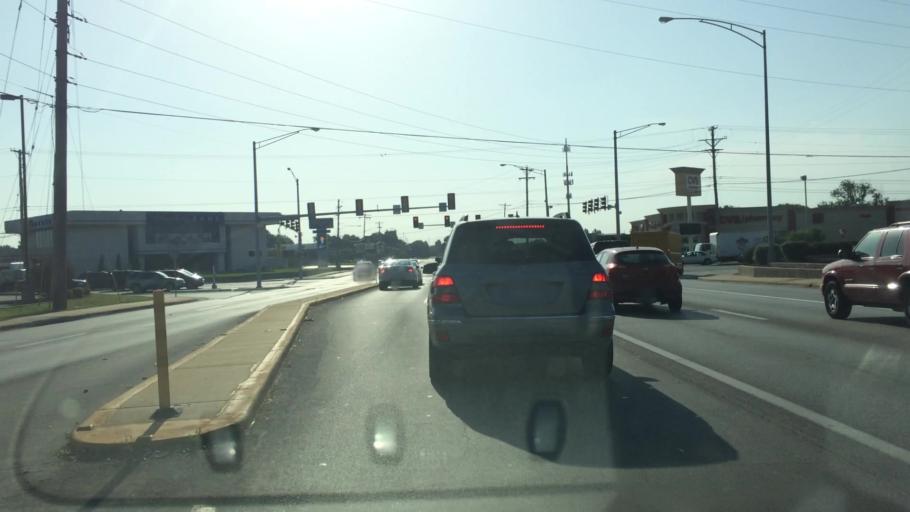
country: US
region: Missouri
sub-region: Greene County
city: Springfield
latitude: 37.1599
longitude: -93.2964
